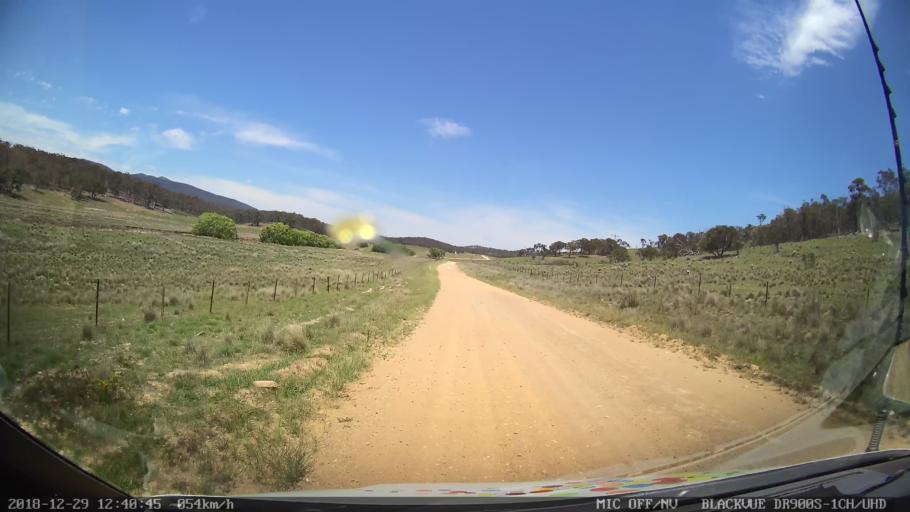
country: AU
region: Australian Capital Territory
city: Macarthur
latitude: -35.6037
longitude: 149.2238
